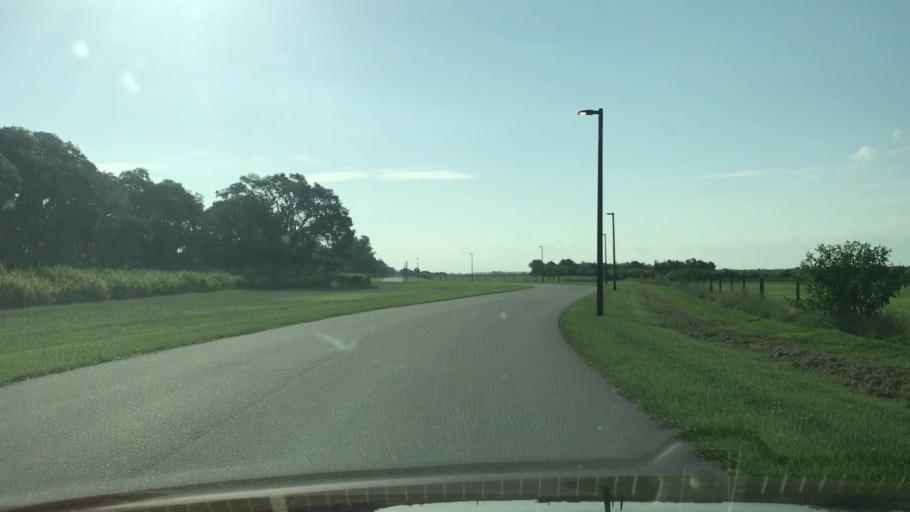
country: US
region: Florida
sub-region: Sarasota County
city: The Meadows
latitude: 27.4716
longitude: -82.3884
